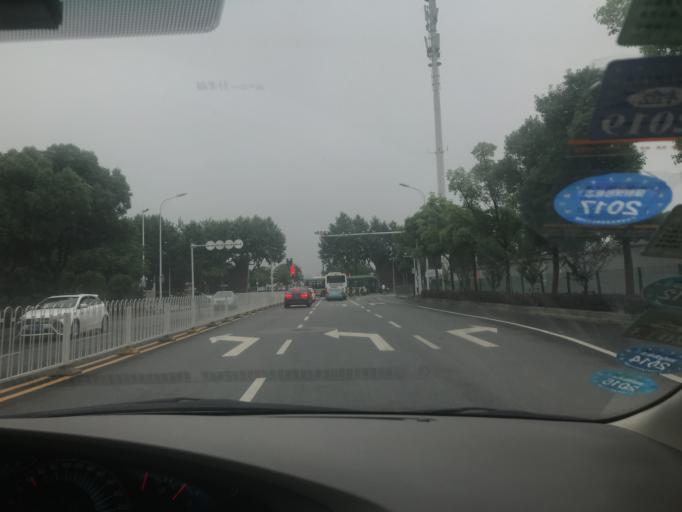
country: CN
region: Hubei
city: Wuhan
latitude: 30.5514
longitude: 114.2737
